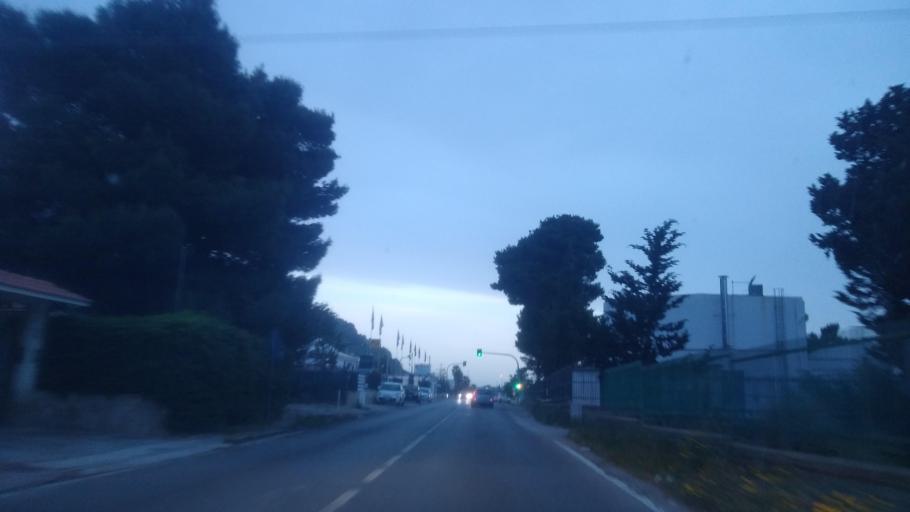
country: IT
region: Sicily
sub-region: Palermo
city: Terrasini
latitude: 38.1456
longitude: 13.0888
